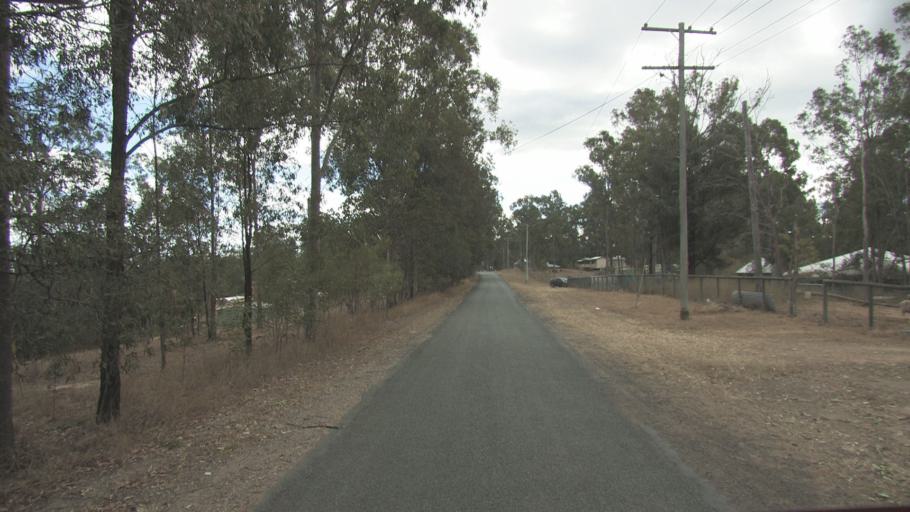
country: AU
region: Queensland
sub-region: Logan
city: Cedar Vale
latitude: -27.8822
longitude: 153.0365
